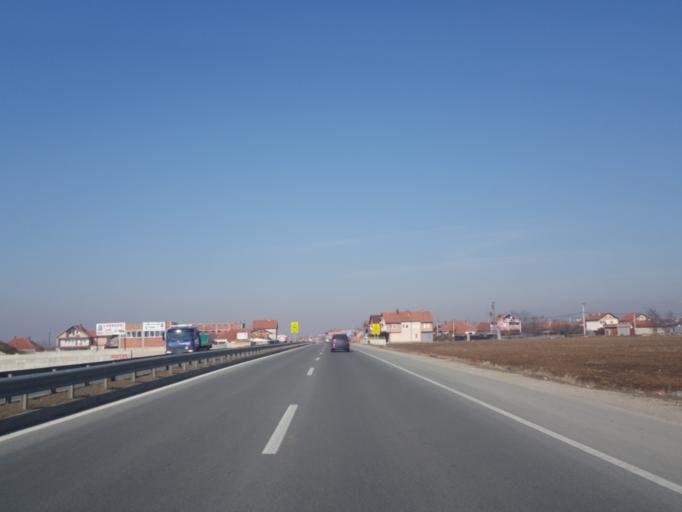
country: XK
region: Pristina
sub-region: Komuna e Obiliqit
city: Obiliq
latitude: 42.7436
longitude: 21.0491
